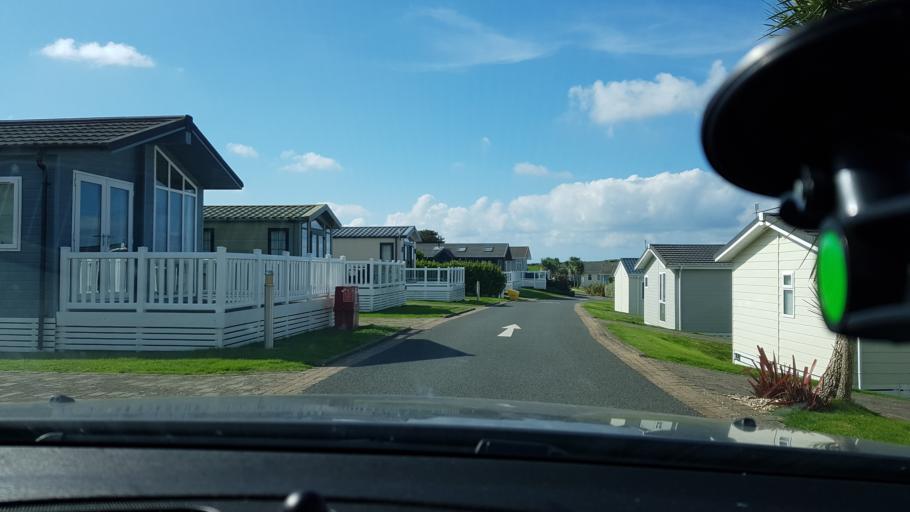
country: GB
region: England
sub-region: Cornwall
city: Tintagel
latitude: 50.6685
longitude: -4.7406
